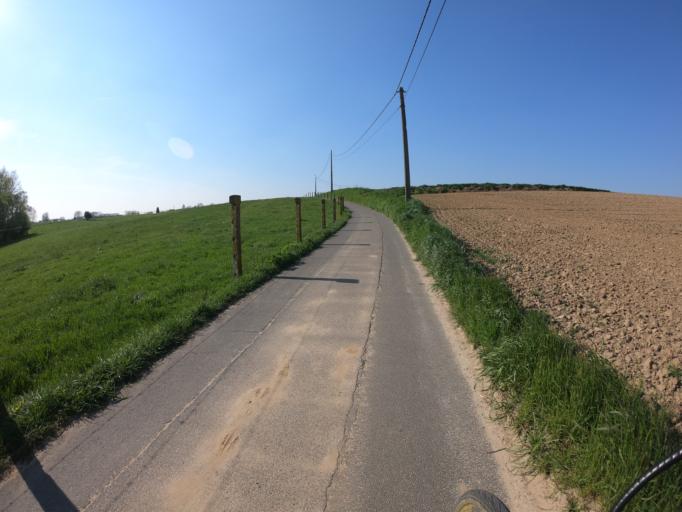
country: BE
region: Flanders
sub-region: Provincie Oost-Vlaanderen
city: Ninove
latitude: 50.8301
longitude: 4.0002
